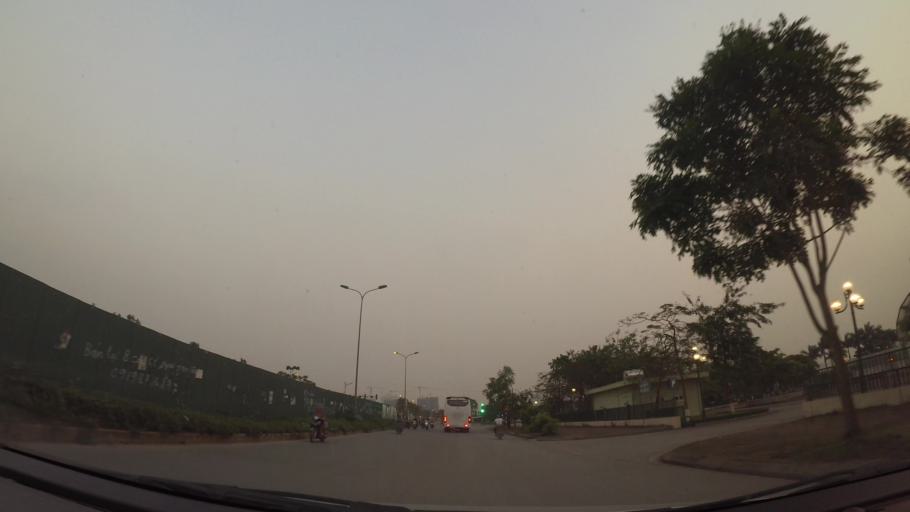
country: VN
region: Ha Noi
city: Tay Ho
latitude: 21.0635
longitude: 105.7899
